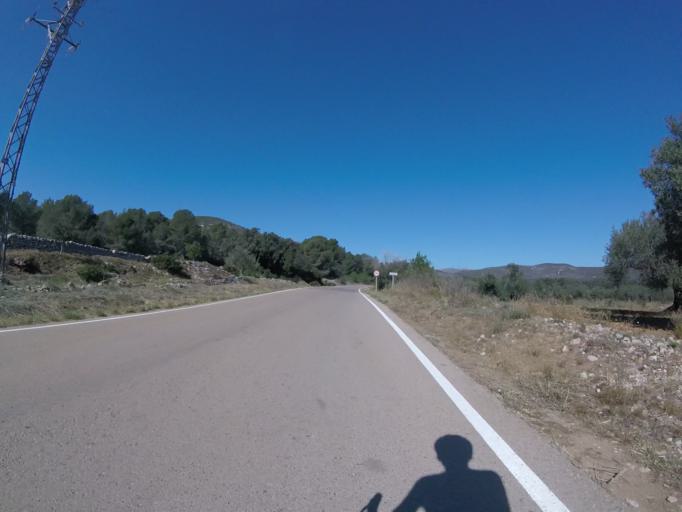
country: ES
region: Valencia
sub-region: Provincia de Castello
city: Santa Magdalena de Pulpis
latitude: 40.3642
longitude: 0.2790
